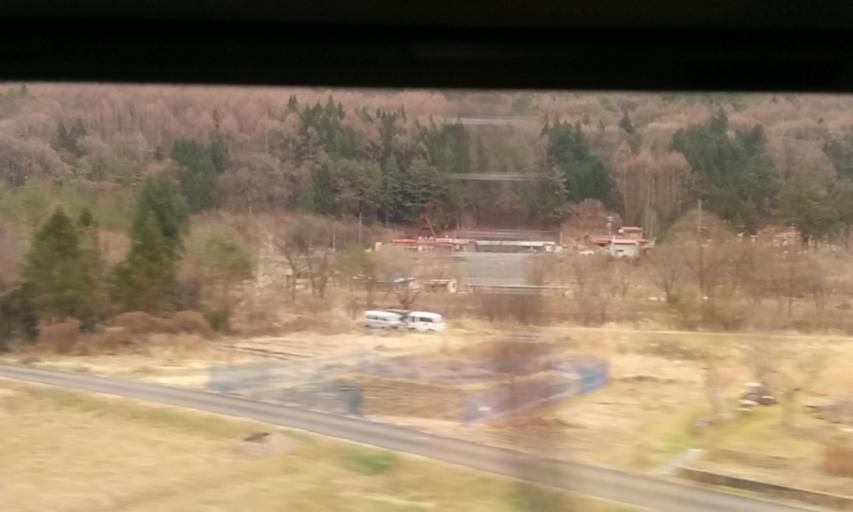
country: JP
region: Nagano
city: Ina
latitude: 35.9136
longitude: 137.7682
